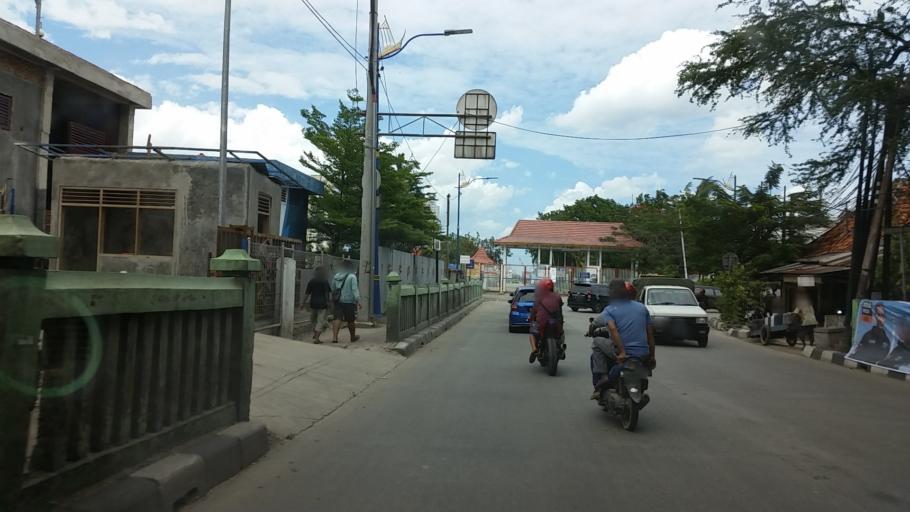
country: ID
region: Jakarta Raya
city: Jakarta
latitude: -6.1265
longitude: 106.8098
